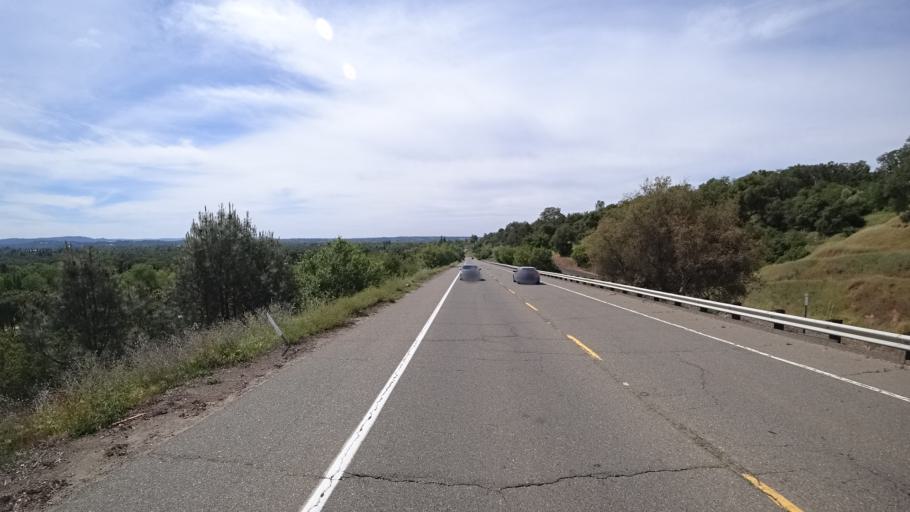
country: US
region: California
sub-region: Placer County
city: Loomis
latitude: 38.8404
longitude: -121.2202
